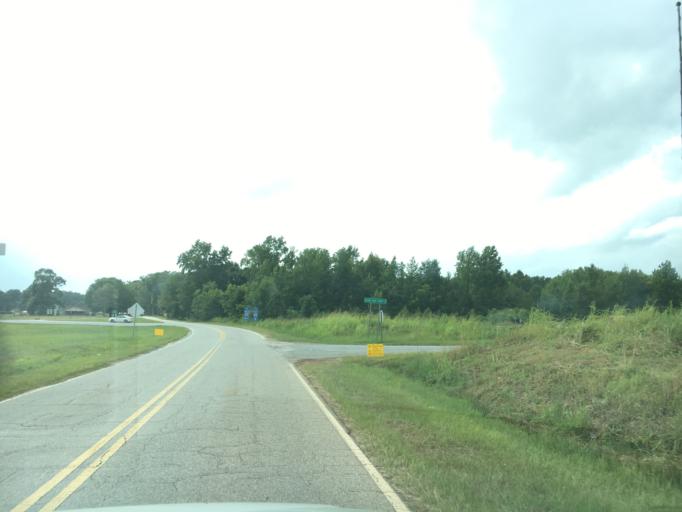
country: US
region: South Carolina
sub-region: Anderson County
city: Williamston
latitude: 34.6669
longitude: -82.5159
